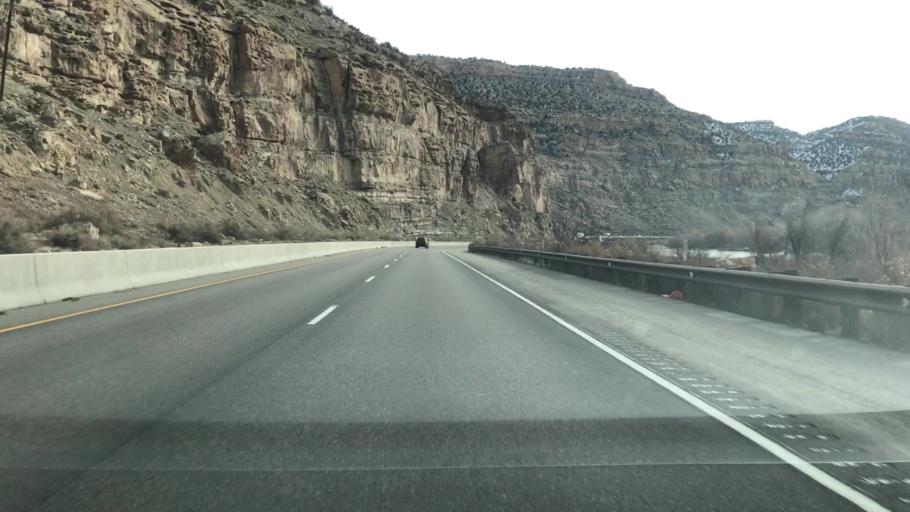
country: US
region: Colorado
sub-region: Mesa County
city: Palisade
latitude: 39.2300
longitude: -108.2677
